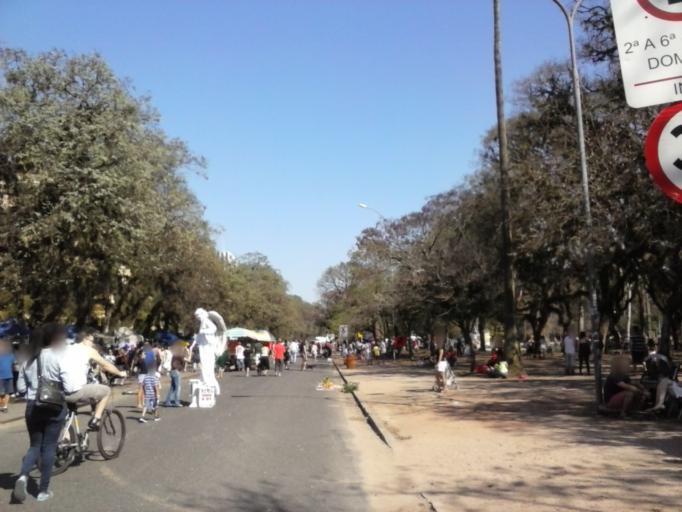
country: BR
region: Rio Grande do Sul
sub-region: Porto Alegre
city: Porto Alegre
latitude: -30.0379
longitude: -51.2131
